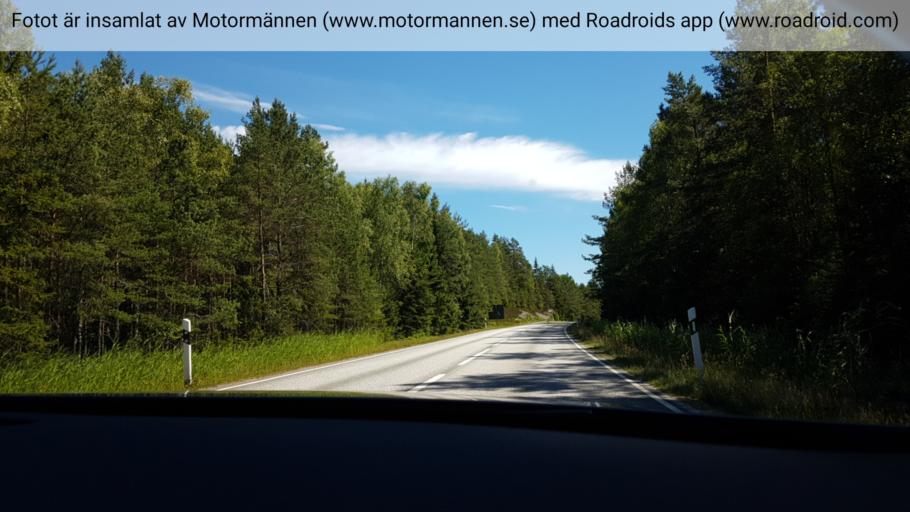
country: SE
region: Joenkoeping
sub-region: Gnosjo Kommun
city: Gnosjoe
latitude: 57.3766
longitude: 13.7362
